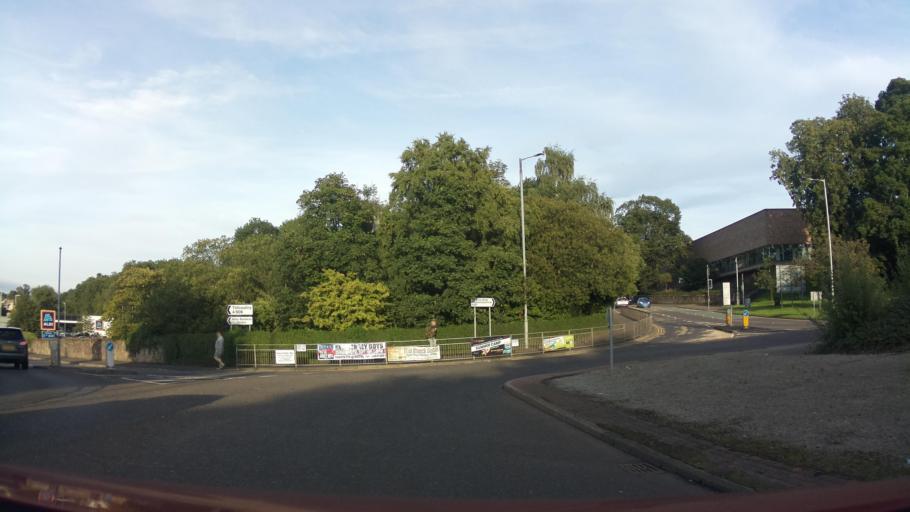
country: GB
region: Scotland
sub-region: Clackmannanshire
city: Alloa
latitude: 56.1168
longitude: -3.7874
